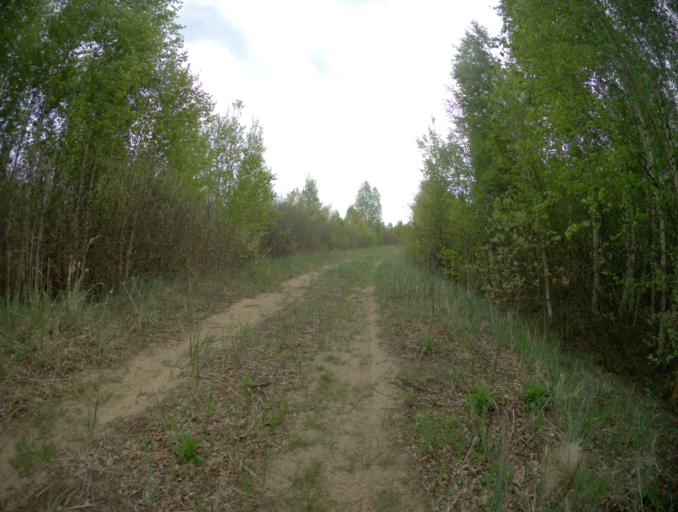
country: RU
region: Vladimir
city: Urshel'skiy
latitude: 55.6053
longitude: 40.1591
